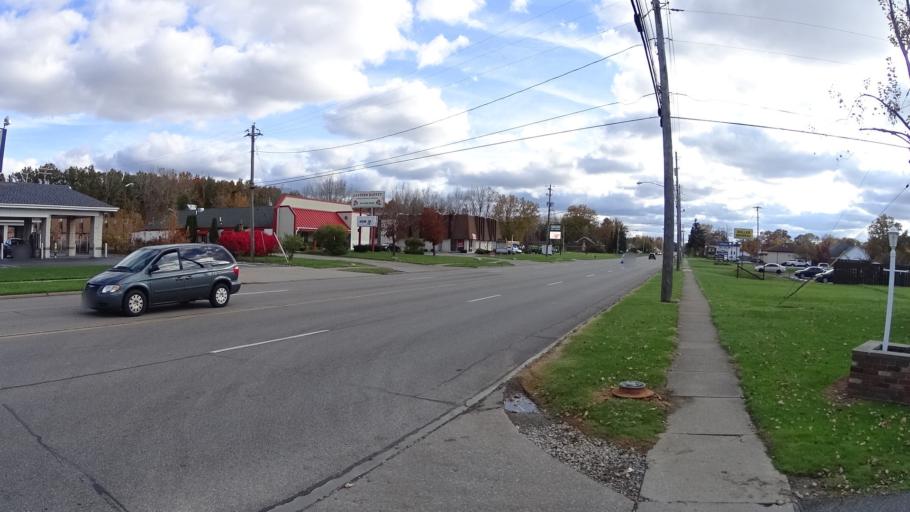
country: US
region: Ohio
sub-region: Lorain County
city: Lorain
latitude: 41.4271
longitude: -82.1857
